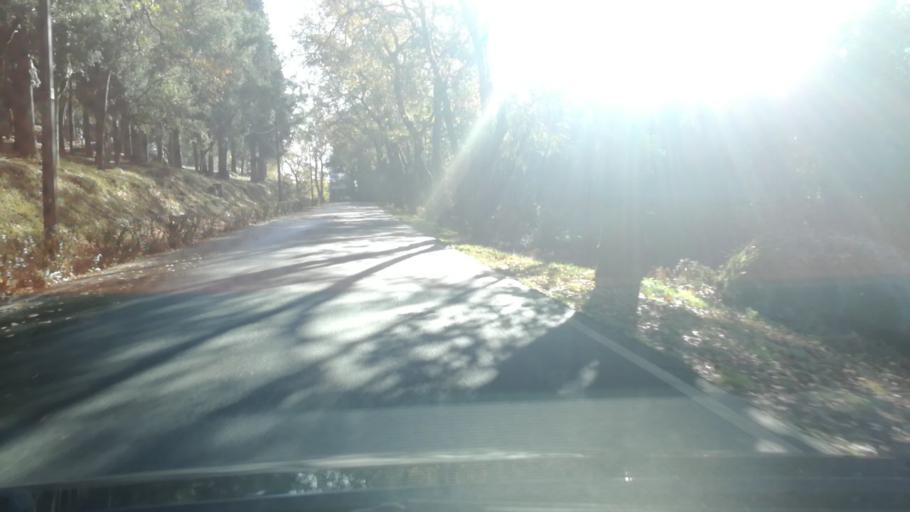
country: PT
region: Braga
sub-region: Braga
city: Braga
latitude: 41.5387
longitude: -8.3707
